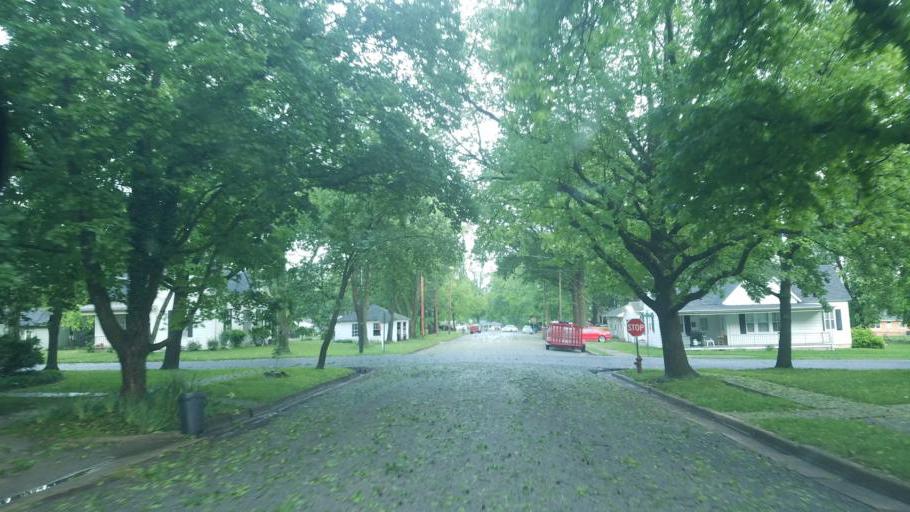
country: US
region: Missouri
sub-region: Moniteau County
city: California
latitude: 38.6256
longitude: -92.5689
